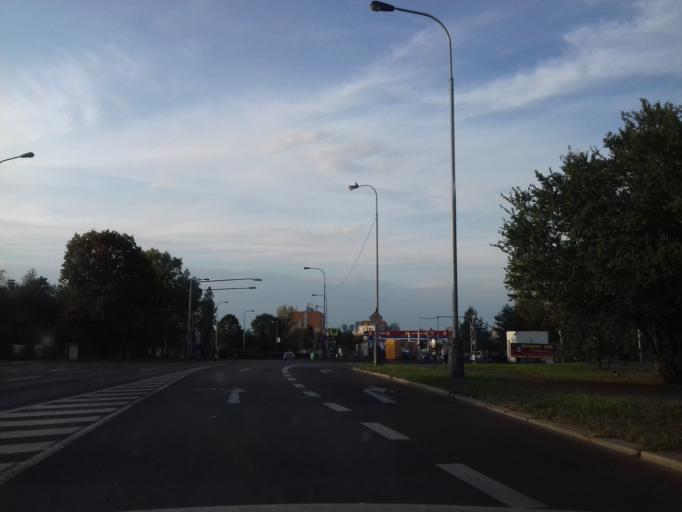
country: CZ
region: Praha
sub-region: Praha 4
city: Hodkovicky
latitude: 50.0193
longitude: 14.4526
